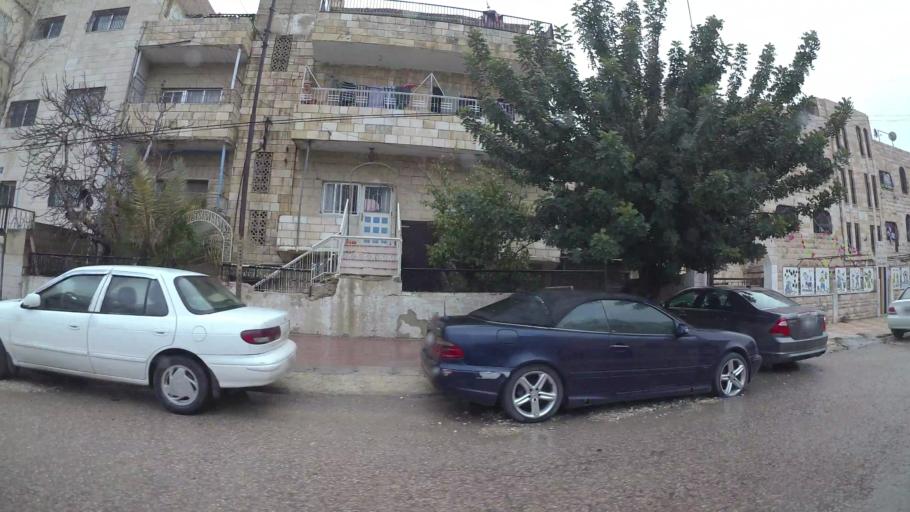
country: JO
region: Amman
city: Amman
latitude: 31.9697
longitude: 35.9228
